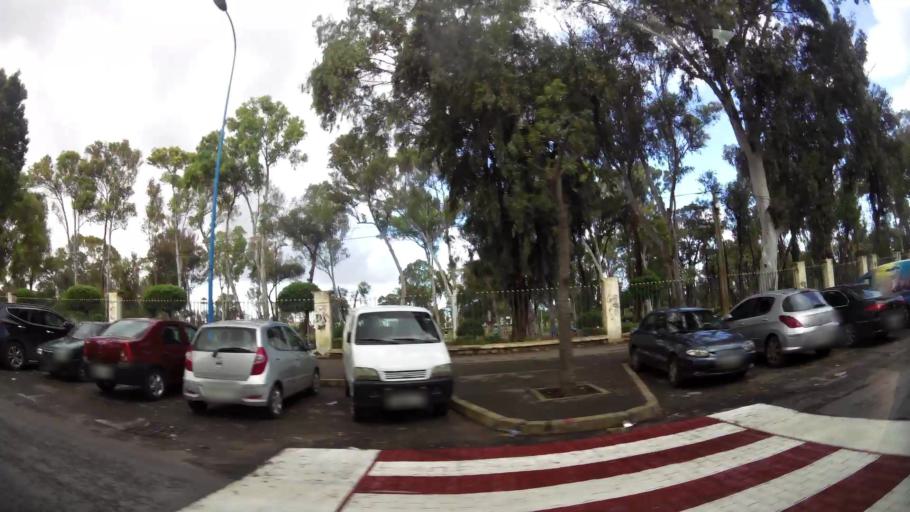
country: MA
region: Grand Casablanca
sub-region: Casablanca
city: Casablanca
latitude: 33.5646
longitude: -7.6116
